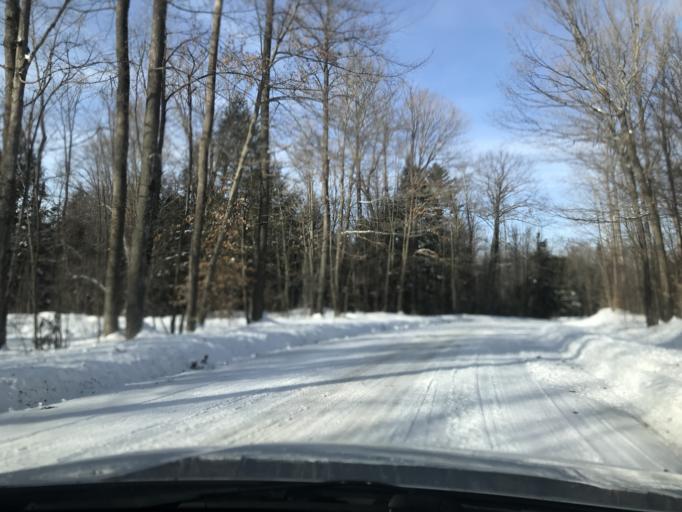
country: US
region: Wisconsin
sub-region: Oconto County
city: Gillett
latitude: 45.1464
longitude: -88.2348
